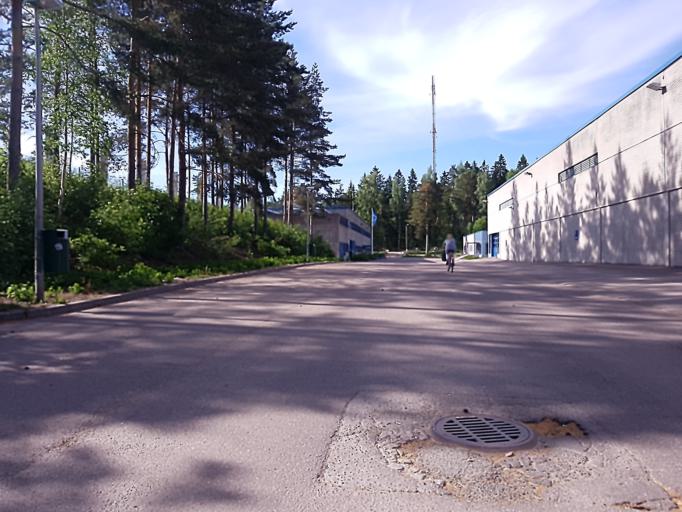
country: FI
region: Uusimaa
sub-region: Helsinki
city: Helsinki
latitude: 60.2340
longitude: 24.9609
